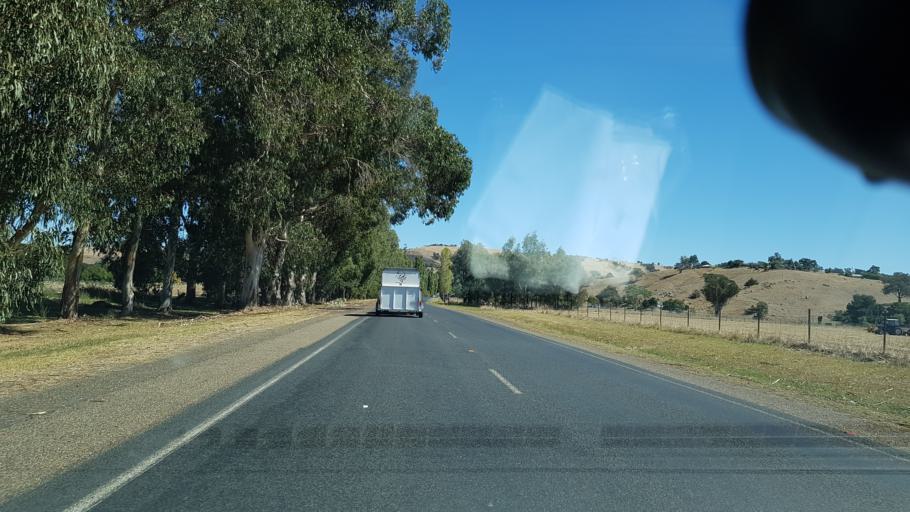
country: AU
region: New South Wales
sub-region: Gundagai
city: Gundagai
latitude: -34.8228
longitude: 148.3363
